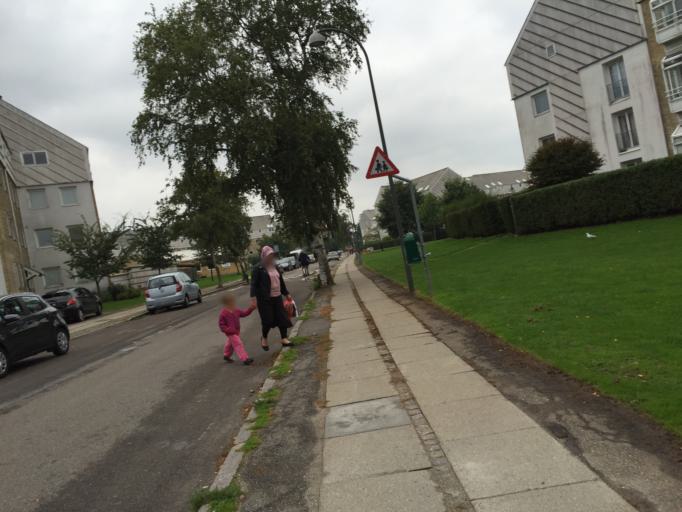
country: DK
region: Capital Region
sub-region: Herlev Kommune
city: Herlev
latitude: 55.7212
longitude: 12.4365
